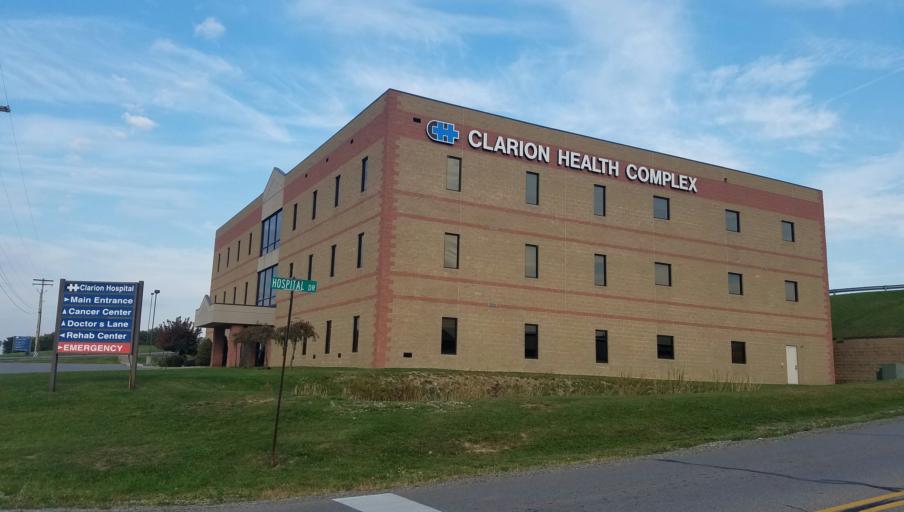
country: US
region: Pennsylvania
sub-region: Clarion County
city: Clarion
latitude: 41.1898
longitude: -79.3974
